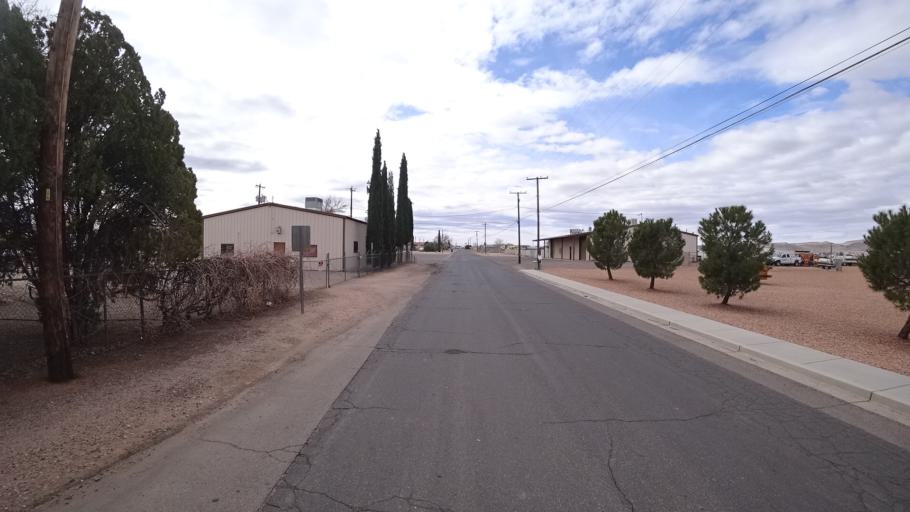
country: US
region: Arizona
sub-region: Mohave County
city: New Kingman-Butler
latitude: 35.2308
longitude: -114.0004
